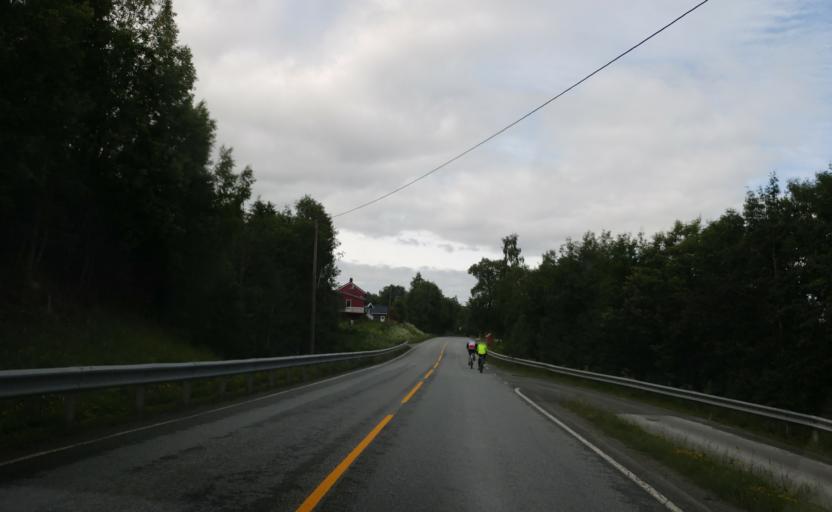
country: NO
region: Nord-Trondelag
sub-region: Stjordal
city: Stjordalshalsen
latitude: 63.4013
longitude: 10.9460
